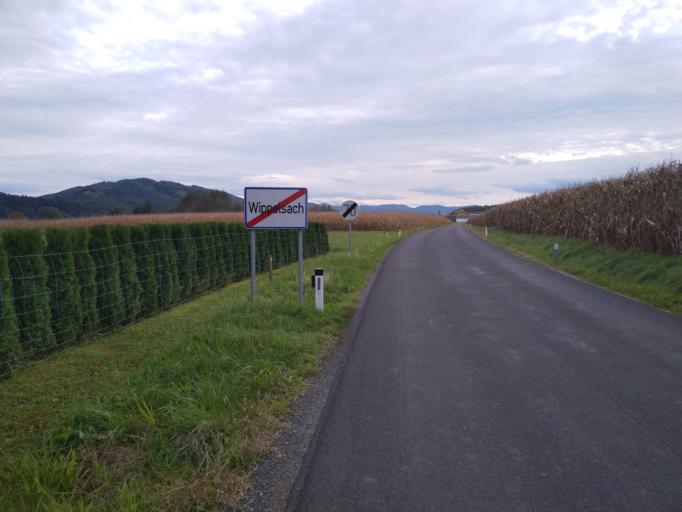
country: AT
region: Styria
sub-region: Politischer Bezirk Leibnitz
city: Grossklein
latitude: 46.7459
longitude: 15.4342
